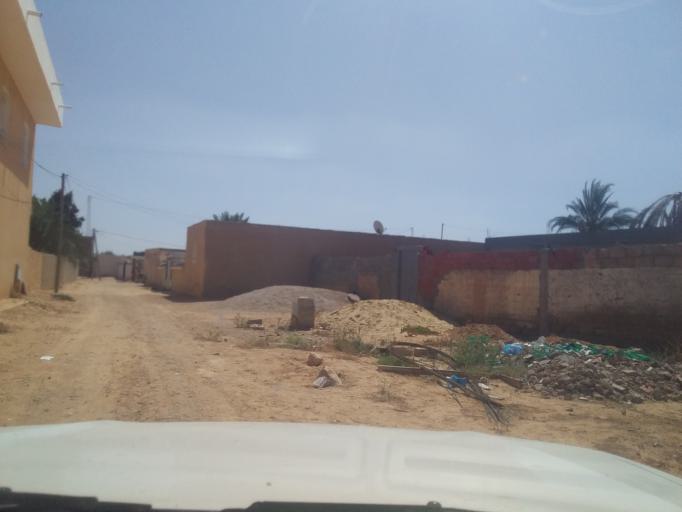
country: TN
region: Qabis
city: Matmata
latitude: 33.5920
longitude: 10.2831
